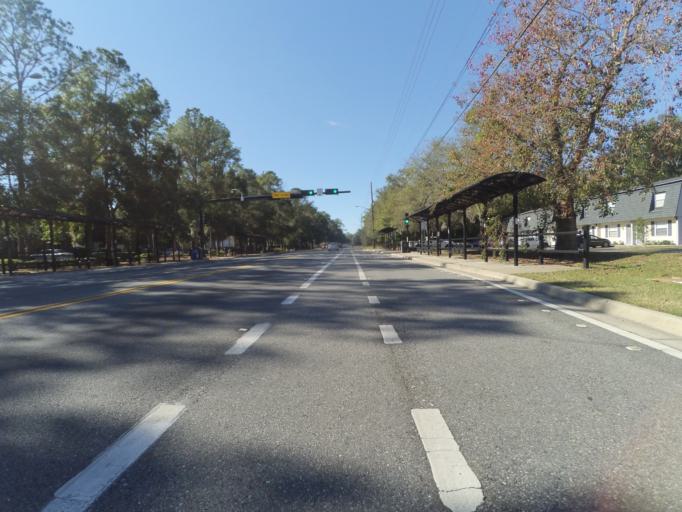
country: US
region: Florida
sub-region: Alachua County
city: Gainesville
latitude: 29.6341
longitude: -82.3773
